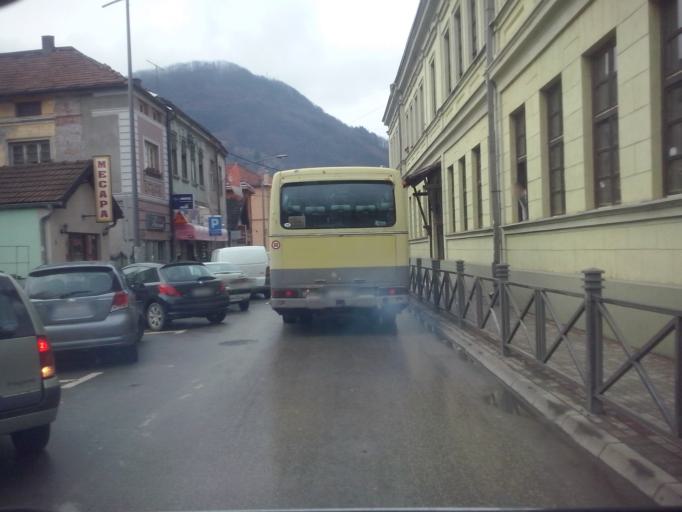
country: RS
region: Central Serbia
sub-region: Moravicki Okrug
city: Ivanjica
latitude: 43.5813
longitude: 20.2290
